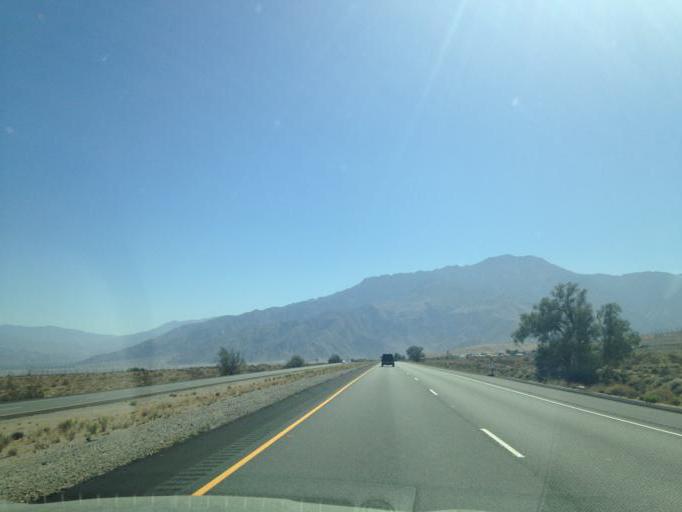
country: US
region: California
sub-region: San Bernardino County
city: Morongo Valley
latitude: 33.9730
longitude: -116.5870
